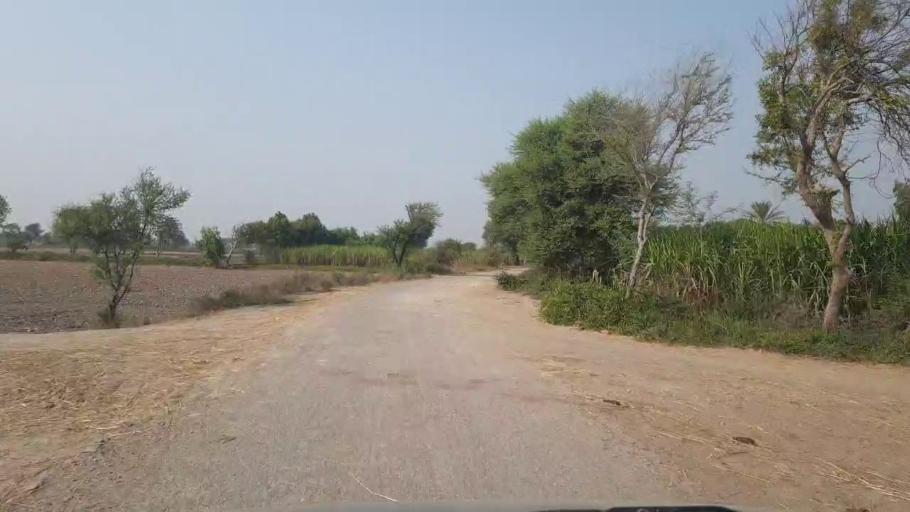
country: PK
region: Sindh
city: Tando Muhammad Khan
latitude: 25.0838
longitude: 68.3412
